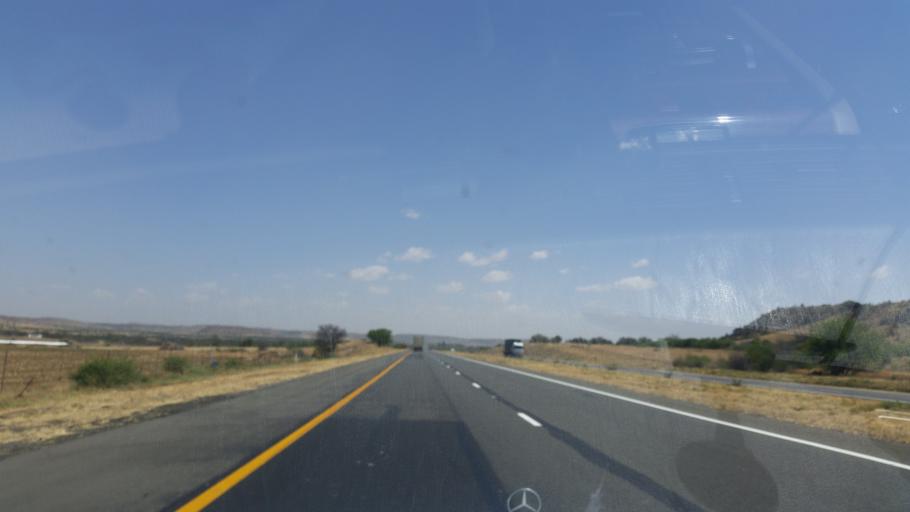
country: ZA
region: Orange Free State
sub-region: Mangaung Metropolitan Municipality
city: Bloemfontein
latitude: -28.9551
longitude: 26.3844
